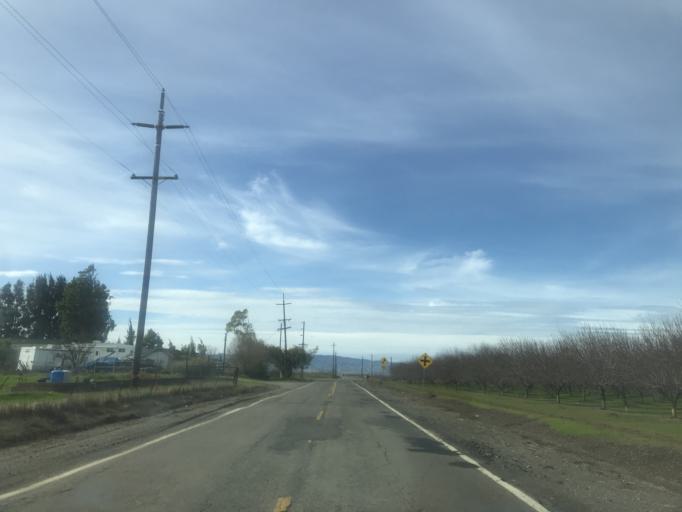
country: US
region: California
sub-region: Yolo County
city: Cottonwood
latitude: 38.6636
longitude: -121.8931
